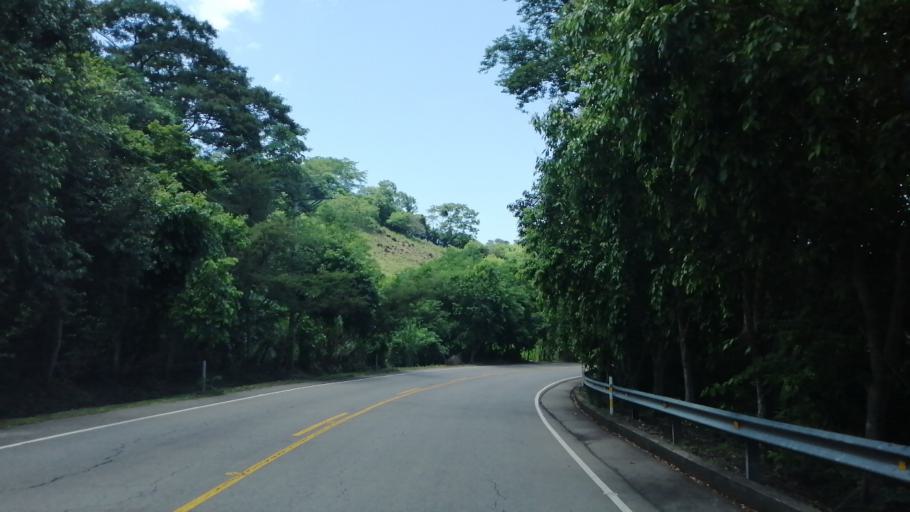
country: SV
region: Chalatenango
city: Nueva Concepcion
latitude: 14.1820
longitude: -89.3233
